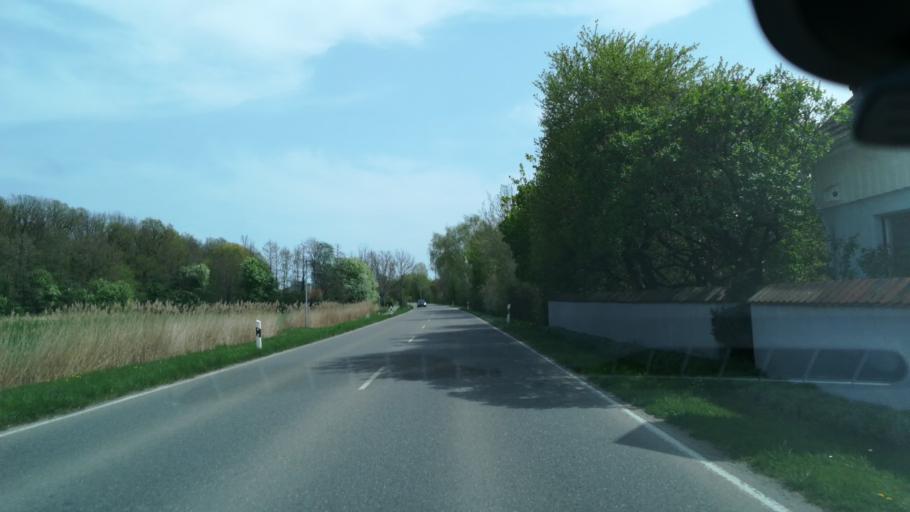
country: DE
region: Baden-Wuerttemberg
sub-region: Freiburg Region
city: Moos
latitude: 47.7498
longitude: 8.9467
